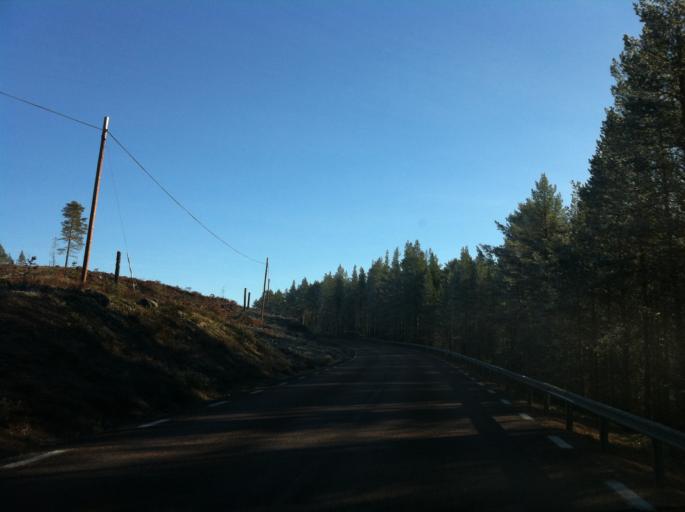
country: NO
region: Hedmark
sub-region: Trysil
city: Innbygda
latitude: 61.8455
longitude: 12.7775
